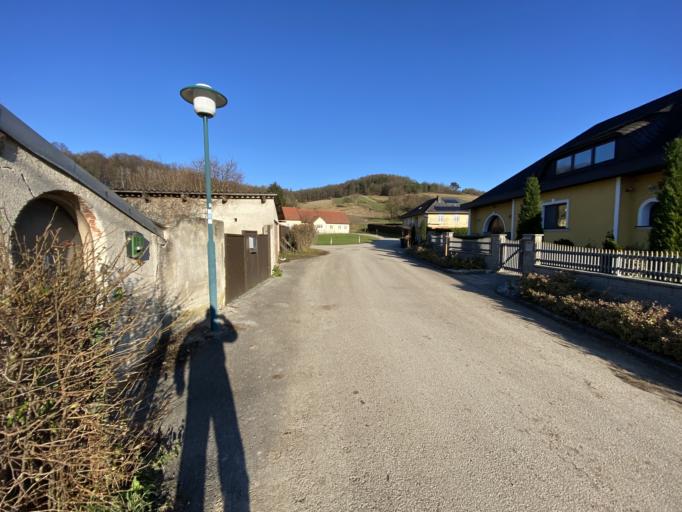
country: AT
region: Lower Austria
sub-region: Politischer Bezirk Sankt Polten
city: Pyhra
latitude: 48.1966
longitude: 15.7118
